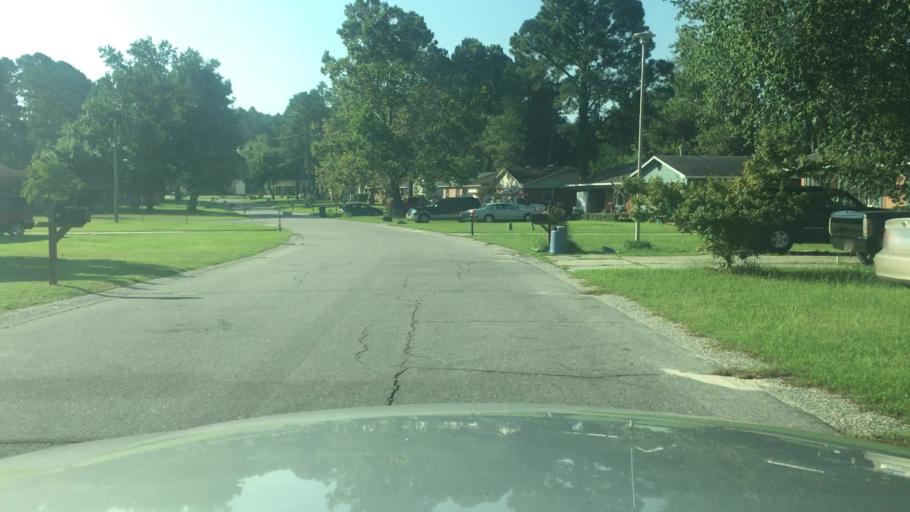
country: US
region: North Carolina
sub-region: Cumberland County
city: Spring Lake
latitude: 35.1571
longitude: -78.9127
